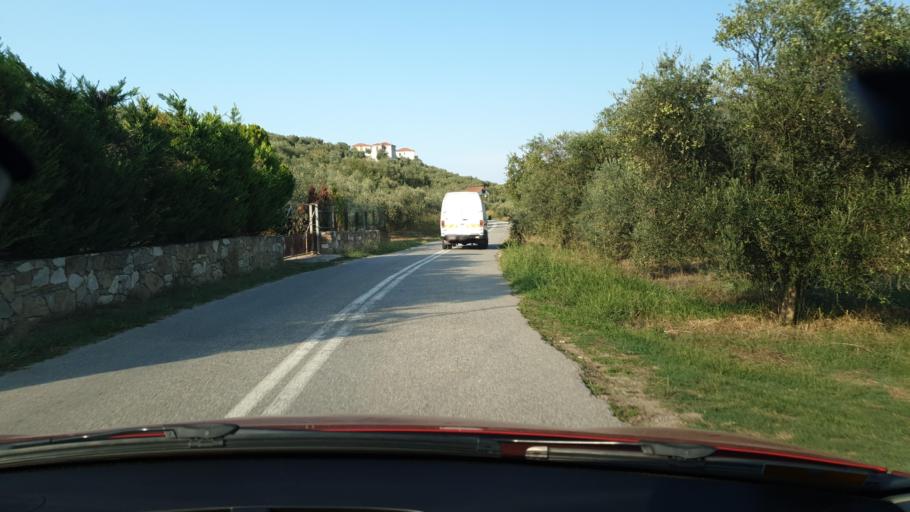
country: GR
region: Thessaly
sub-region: Nomos Magnisias
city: Pteleos
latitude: 38.9991
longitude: 22.9612
